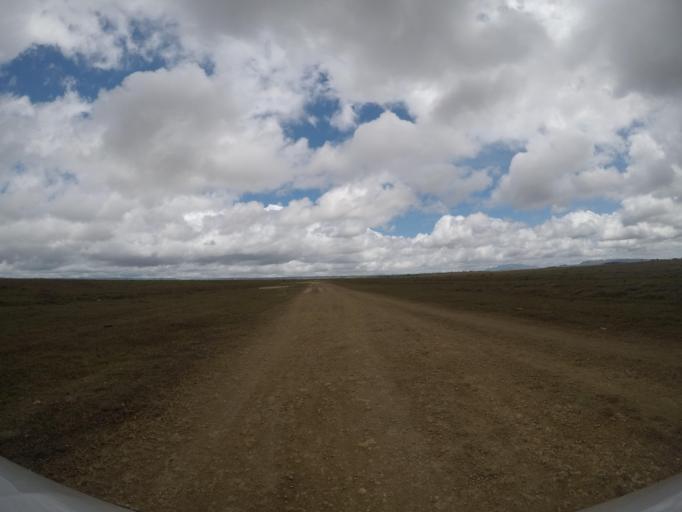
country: TL
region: Lautem
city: Lospalos
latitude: -8.4485
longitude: 126.9875
